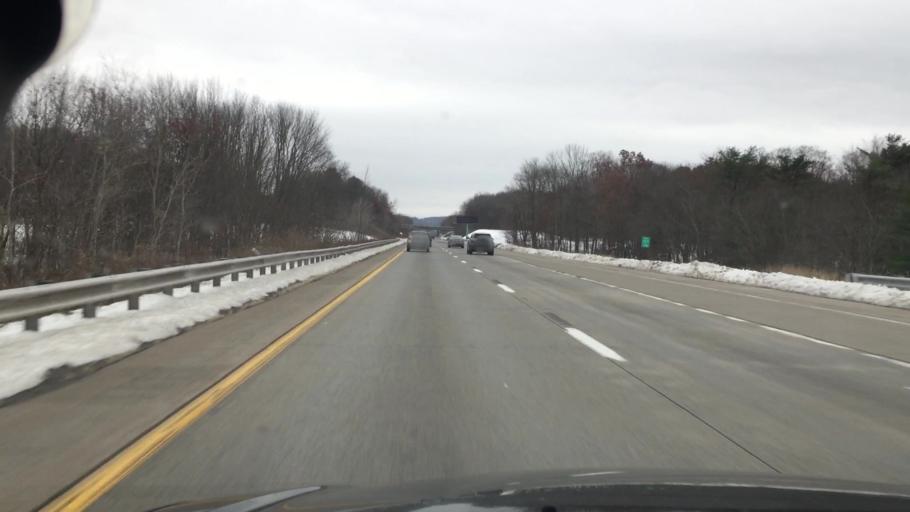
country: US
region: Pennsylvania
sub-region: Luzerne County
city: Nanticoke
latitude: 41.1264
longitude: -75.9626
